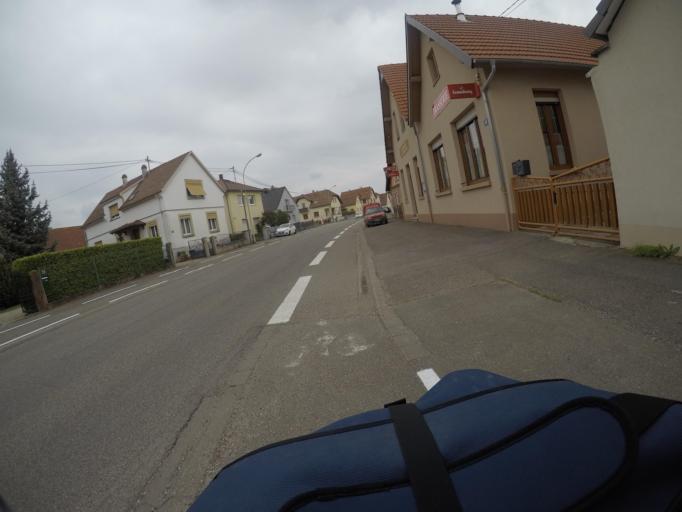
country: FR
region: Alsace
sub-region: Departement du Bas-Rhin
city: Gambsheim
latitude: 48.6891
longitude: 7.8723
